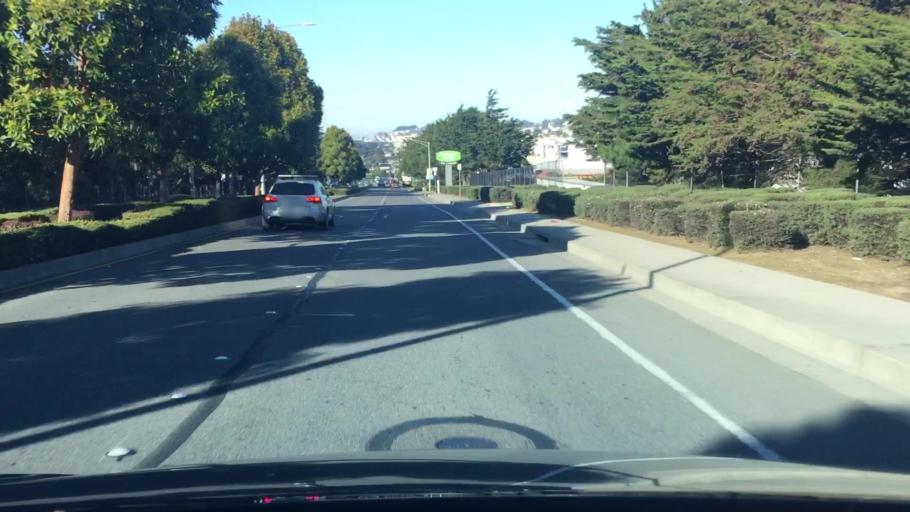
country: US
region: California
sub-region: San Mateo County
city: Colma
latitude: 37.6812
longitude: -122.4706
